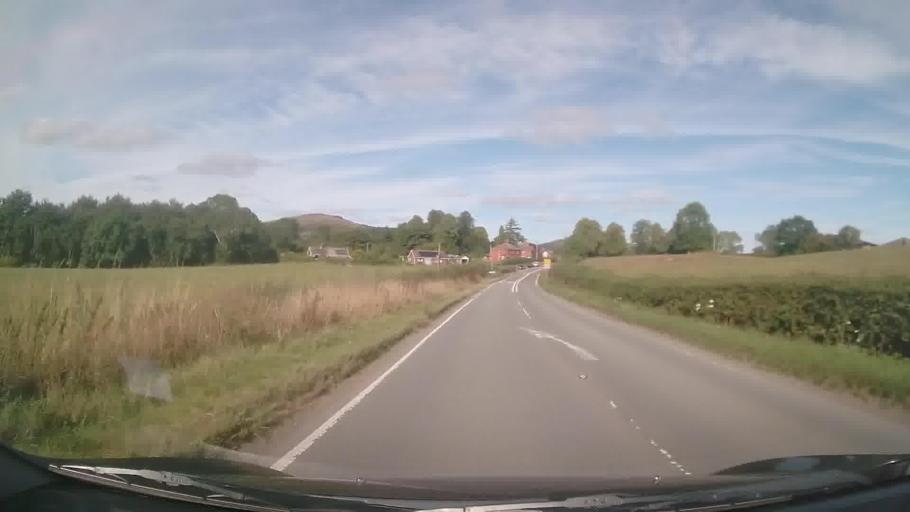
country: GB
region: England
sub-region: Shropshire
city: Lydham
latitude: 52.5106
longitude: -2.9815
